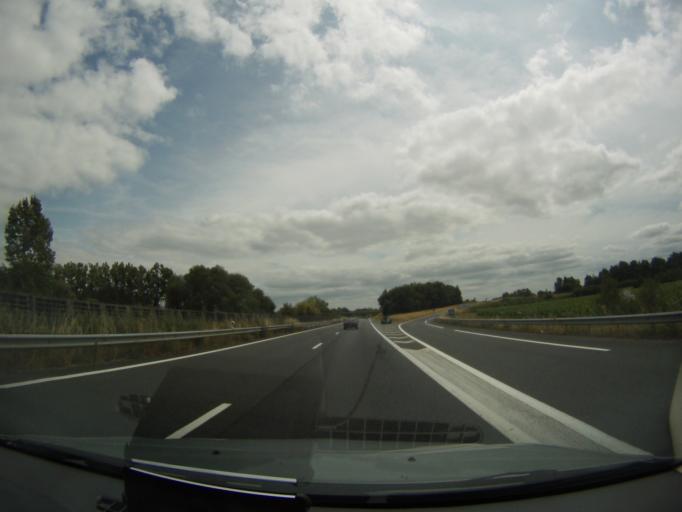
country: FR
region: Pays de la Loire
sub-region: Departement de la Loire-Atlantique
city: Haute-Goulaine
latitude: 47.1827
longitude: -1.4146
